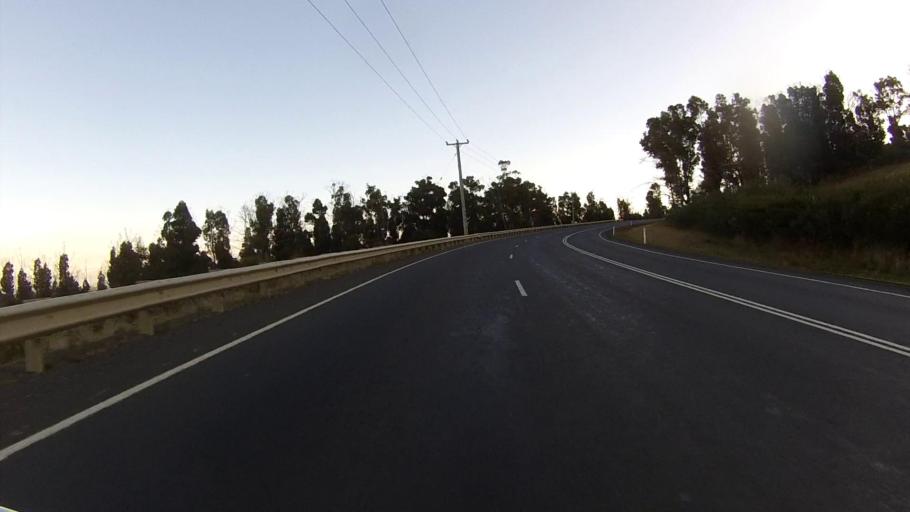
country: AU
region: Tasmania
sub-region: Sorell
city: Sorell
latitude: -42.8239
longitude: 147.7399
